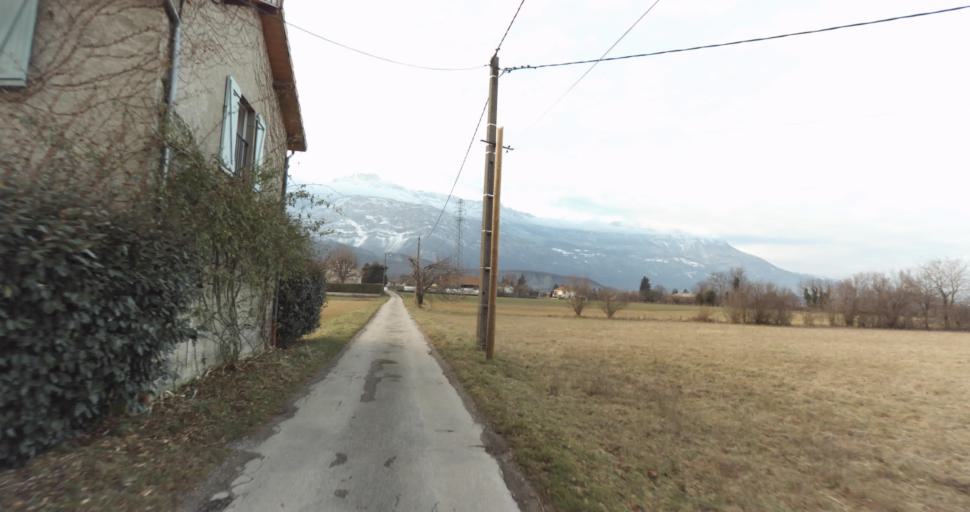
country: FR
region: Rhone-Alpes
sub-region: Departement de l'Isere
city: Vif
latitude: 45.0667
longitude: 5.7002
